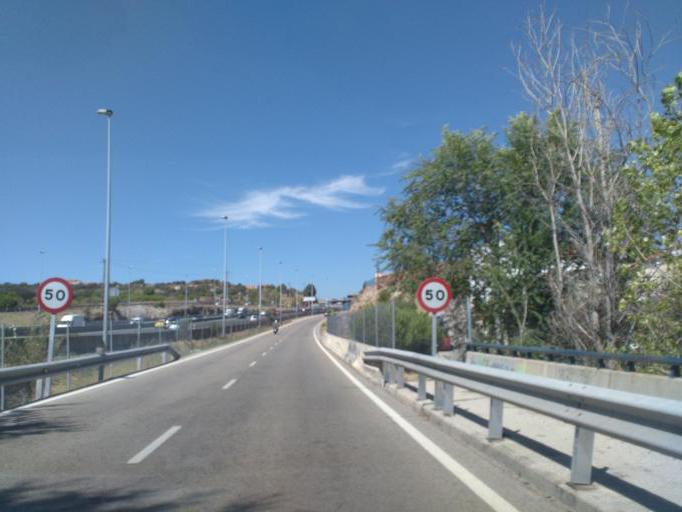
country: ES
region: Madrid
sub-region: Provincia de Madrid
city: Torrelodones
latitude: 40.5751
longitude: -3.9311
